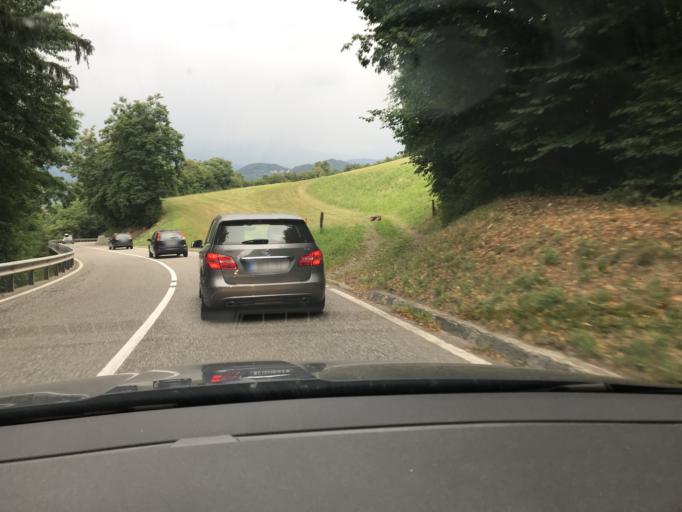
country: IT
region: Trentino-Alto Adige
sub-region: Bolzano
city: Bressanone
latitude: 46.6955
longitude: 11.6595
